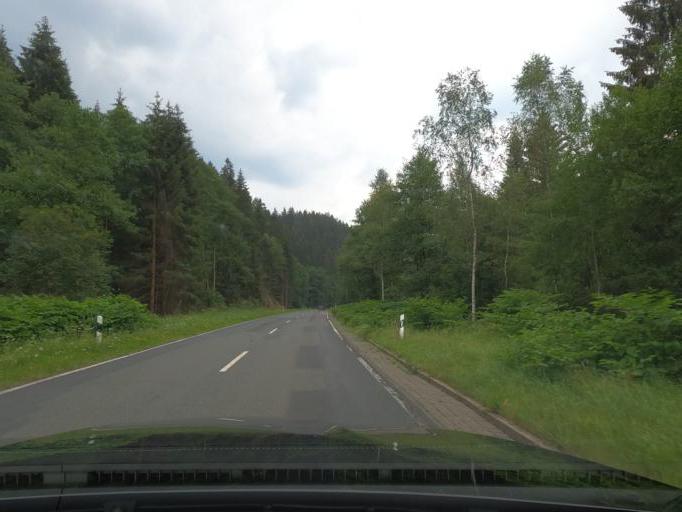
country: DE
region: Lower Saxony
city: Wildemann
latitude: 51.8516
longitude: 10.2742
